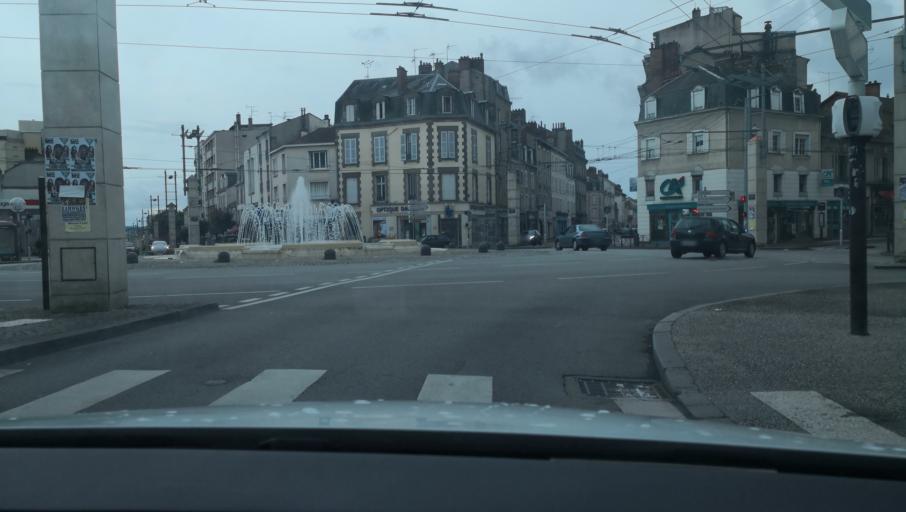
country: FR
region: Limousin
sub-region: Departement de la Haute-Vienne
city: Limoges
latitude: 45.8402
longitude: 1.2574
